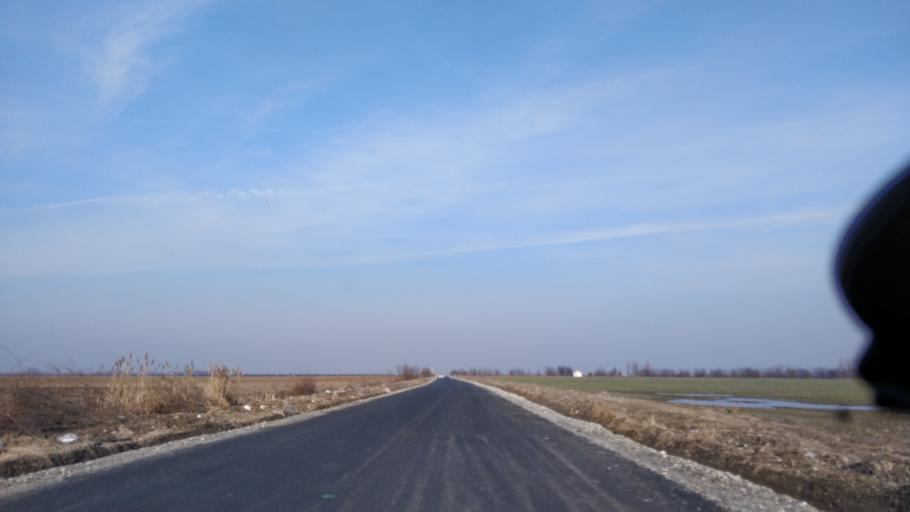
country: RO
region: Dambovita
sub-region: Comuna Brezoaiele
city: Brezoaia
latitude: 44.5317
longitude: 25.7915
